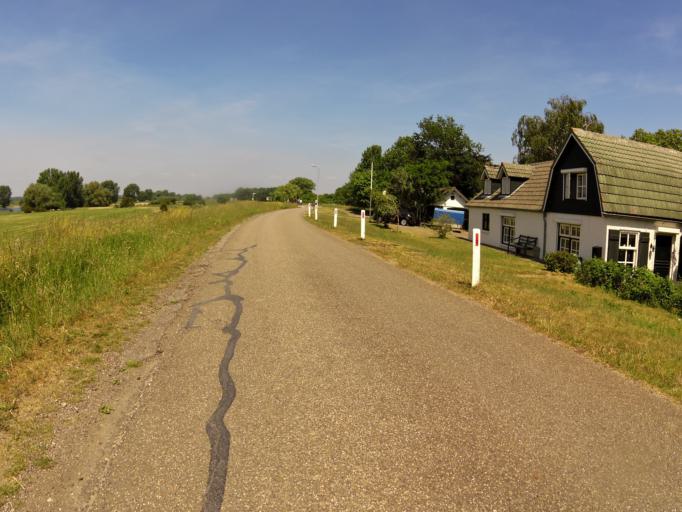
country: NL
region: Gelderland
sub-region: Gemeente Maasdriel
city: Heerewaarden
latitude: 51.7597
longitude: 5.3636
